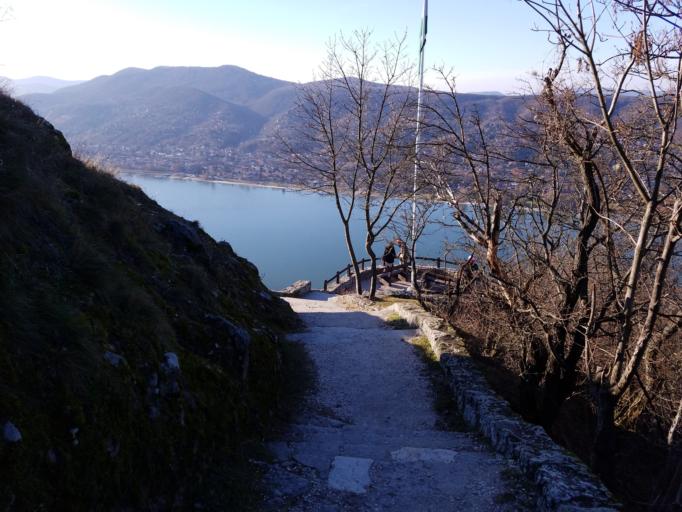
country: HU
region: Pest
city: Visegrad
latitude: 47.7945
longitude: 18.9797
